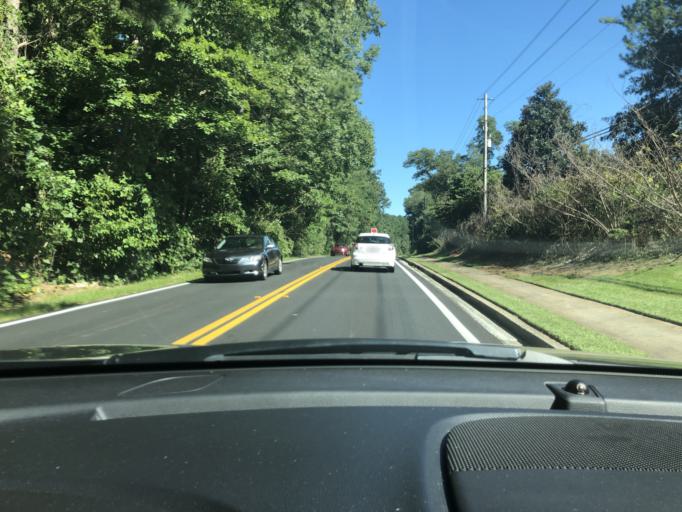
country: US
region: Georgia
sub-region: Gwinnett County
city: Lawrenceville
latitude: 33.9429
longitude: -83.9688
